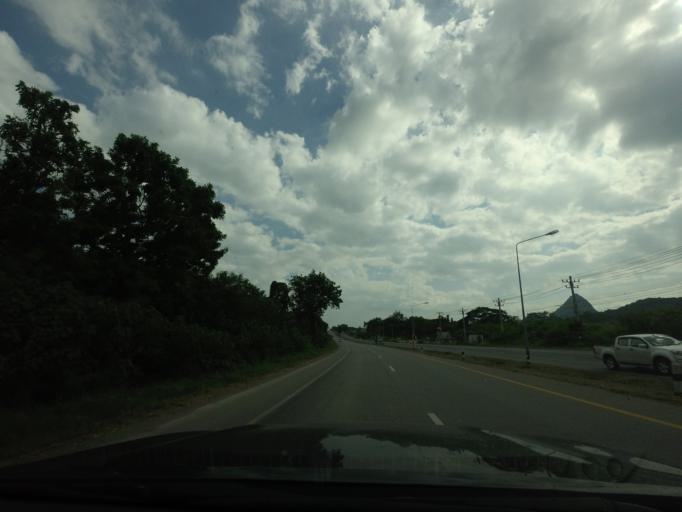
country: TH
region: Lop Buri
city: Chai Badan
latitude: 15.2794
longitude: 101.1239
